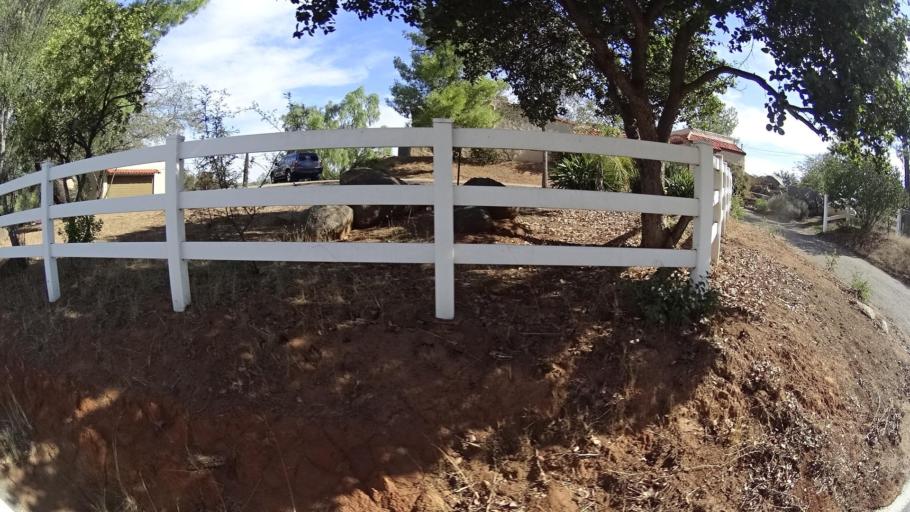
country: US
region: California
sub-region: San Diego County
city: Alpine
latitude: 32.8209
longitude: -116.7858
